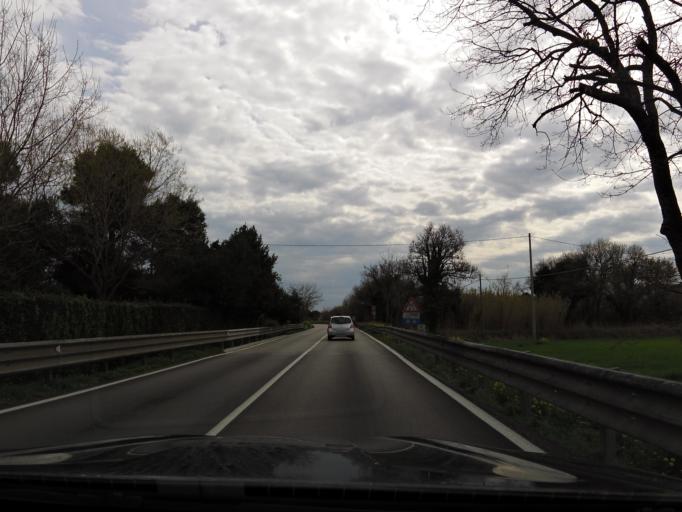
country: IT
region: The Marches
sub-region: Provincia di Macerata
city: Porto Recanati
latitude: 43.3956
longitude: 13.6794
